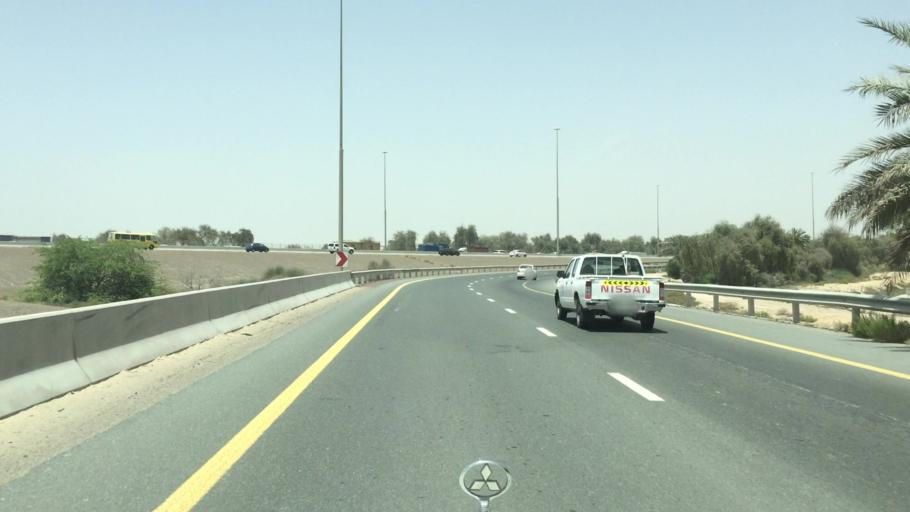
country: AE
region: Dubai
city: Dubai
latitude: 25.1199
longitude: 55.3674
